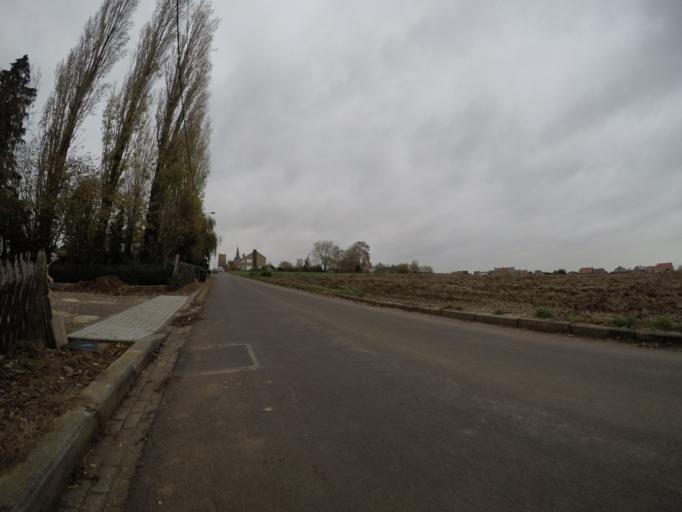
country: BE
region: Flanders
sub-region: Provincie West-Vlaanderen
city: Saint-Yvon
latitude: 50.7827
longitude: 2.8837
